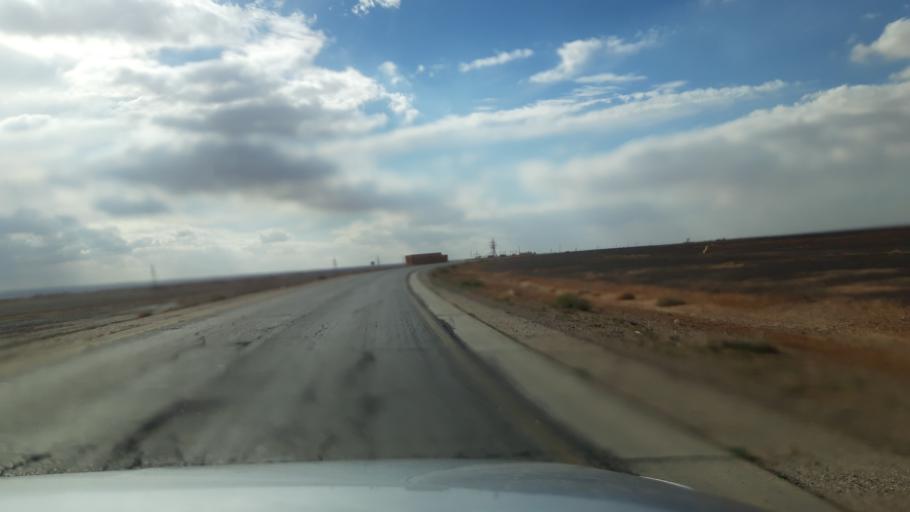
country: JO
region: Amman
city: Al Azraq ash Shamali
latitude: 31.7285
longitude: 36.4699
